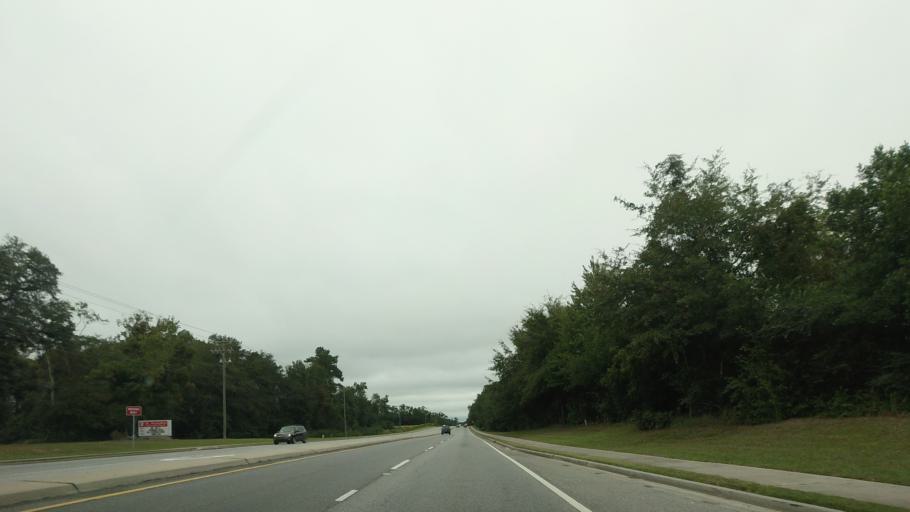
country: US
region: Georgia
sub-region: Lowndes County
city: Valdosta
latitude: 30.8926
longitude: -83.2697
